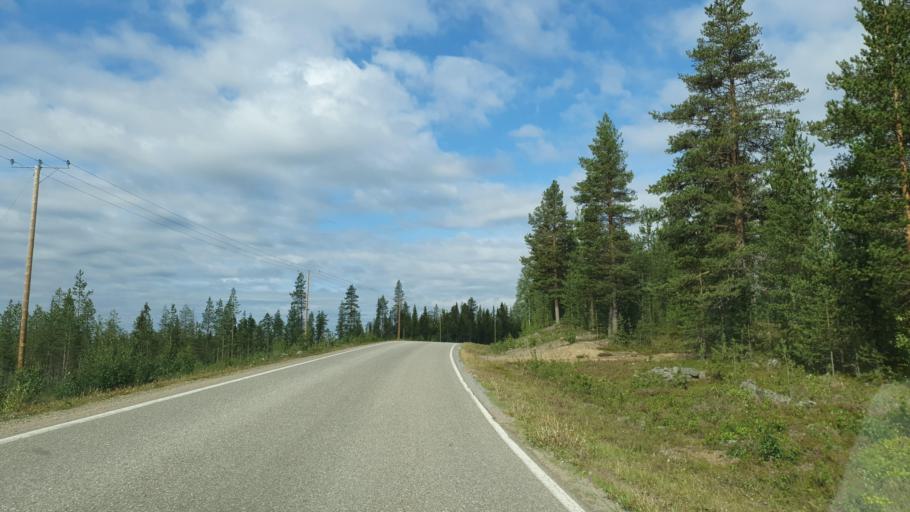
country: FI
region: Lapland
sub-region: Pohjois-Lappi
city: Sodankylae
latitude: 67.5264
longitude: 25.9932
